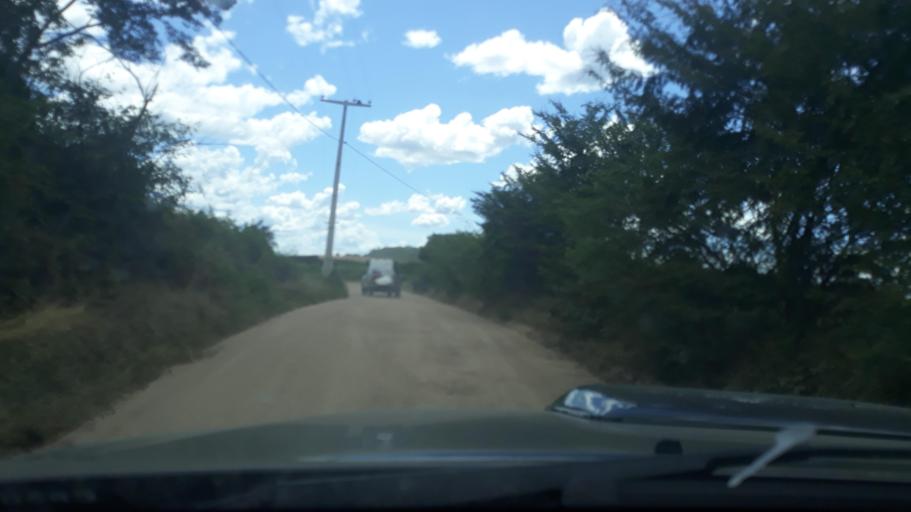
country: BR
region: Bahia
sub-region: Riacho De Santana
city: Riacho de Santana
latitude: -13.9046
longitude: -42.9221
